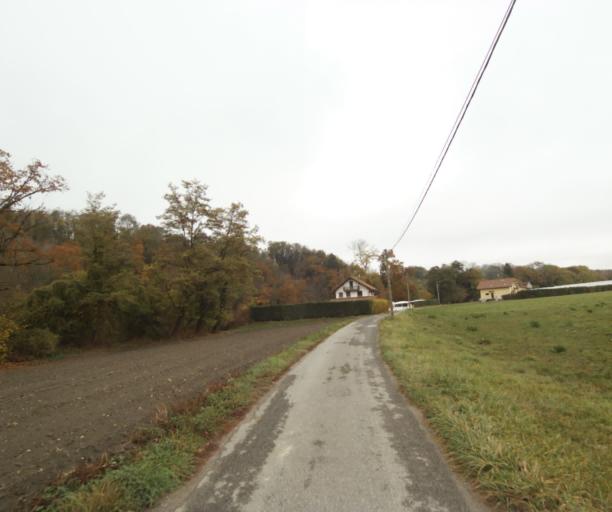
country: FR
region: Rhone-Alpes
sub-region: Departement de la Haute-Savoie
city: Arthaz-Pont-Notre-Dame
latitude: 46.1519
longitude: 6.2752
